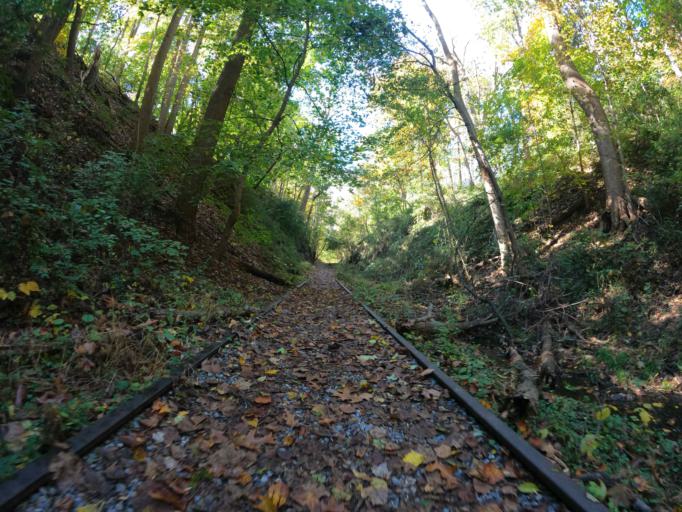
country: US
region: Maryland
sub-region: Carroll County
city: Mount Airy
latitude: 39.3757
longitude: -77.1502
